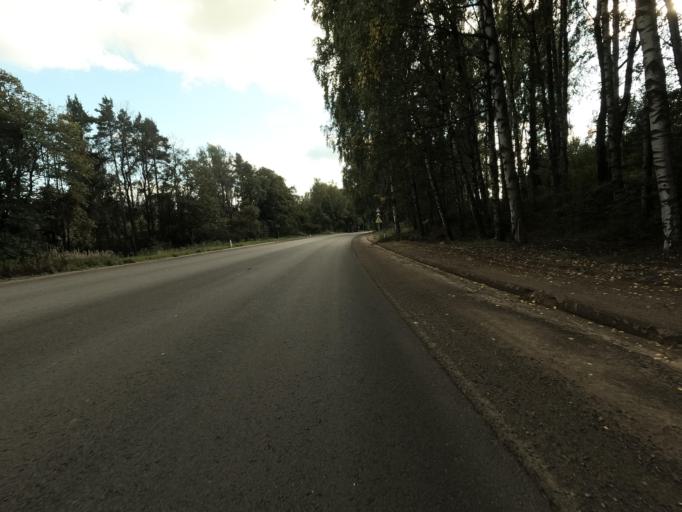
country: RU
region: Leningrad
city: Koltushi
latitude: 59.9466
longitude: 30.6578
